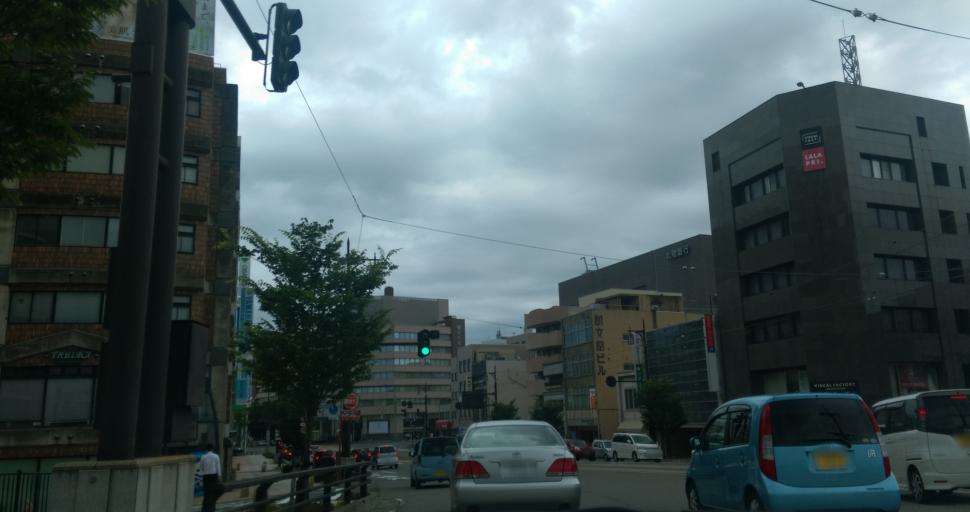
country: JP
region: Fukui
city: Fukui-shi
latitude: 36.0611
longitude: 136.2167
